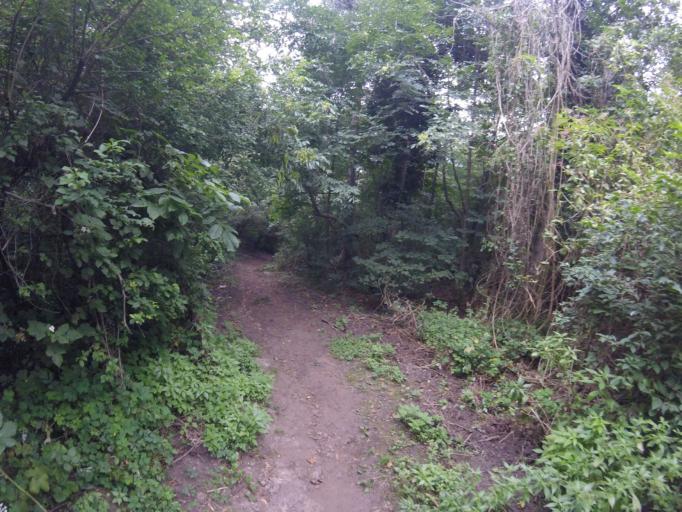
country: HU
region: Veszprem
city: Tapolca
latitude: 46.8453
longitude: 17.4496
